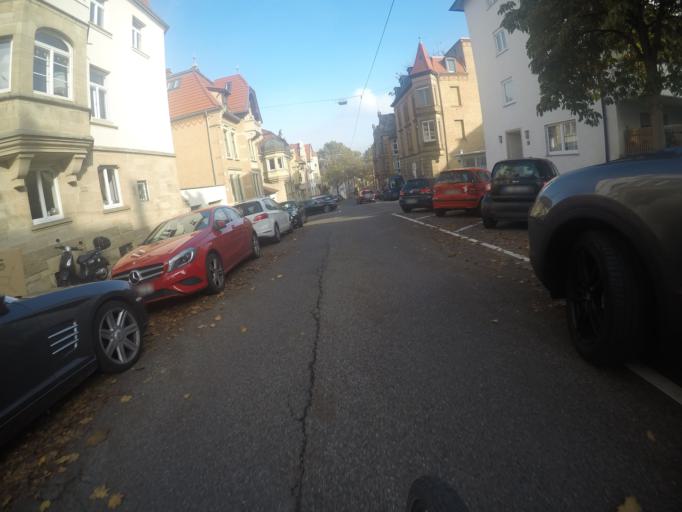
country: DE
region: Baden-Wuerttemberg
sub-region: Regierungsbezirk Stuttgart
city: Stuttgart
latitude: 48.7696
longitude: 9.1835
